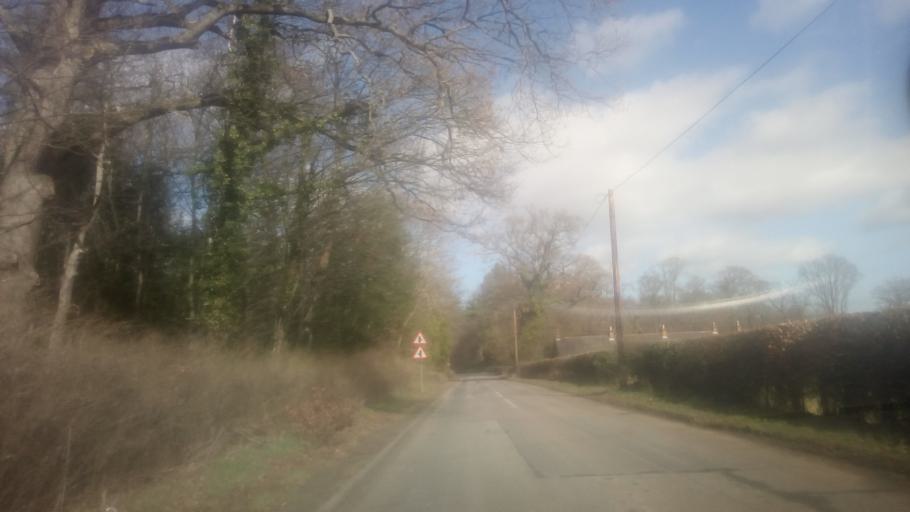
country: GB
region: Scotland
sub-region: Fife
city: Pathhead
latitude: 55.8811
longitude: -2.9600
